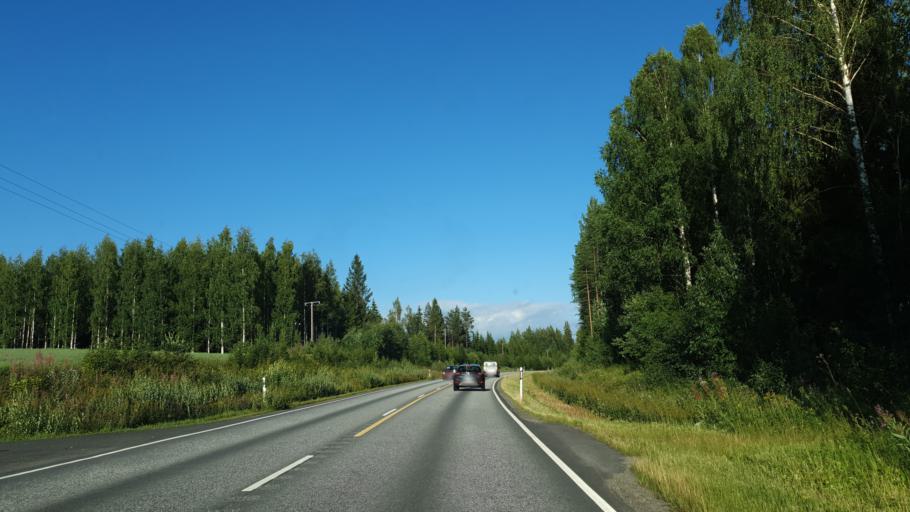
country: FI
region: North Karelia
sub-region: Joensuu
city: Outokumpu
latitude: 62.5347
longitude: 28.9424
